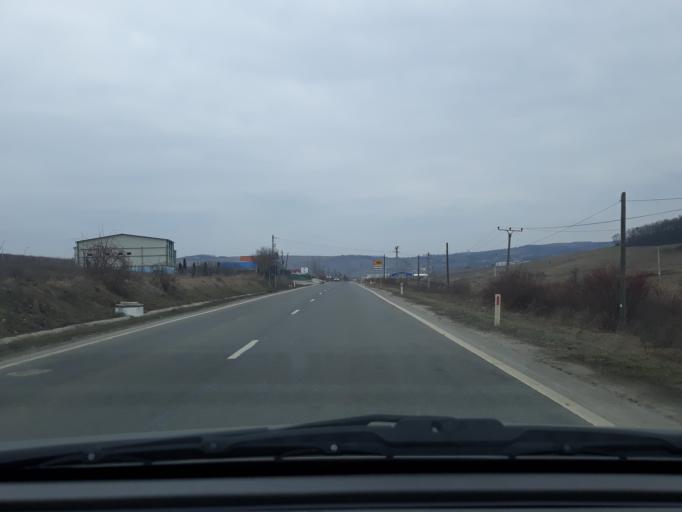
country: RO
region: Salaj
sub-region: Comuna Hereclean
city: Hereclean
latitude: 47.2320
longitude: 22.9766
